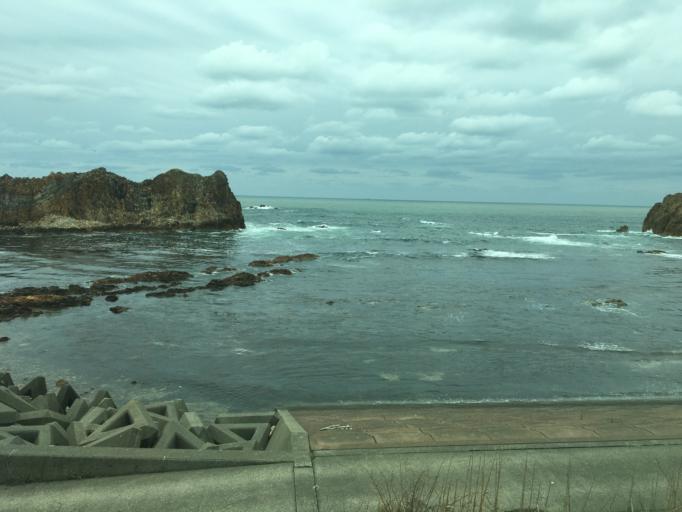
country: JP
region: Aomori
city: Shimokizukuri
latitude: 40.6591
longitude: 139.9375
